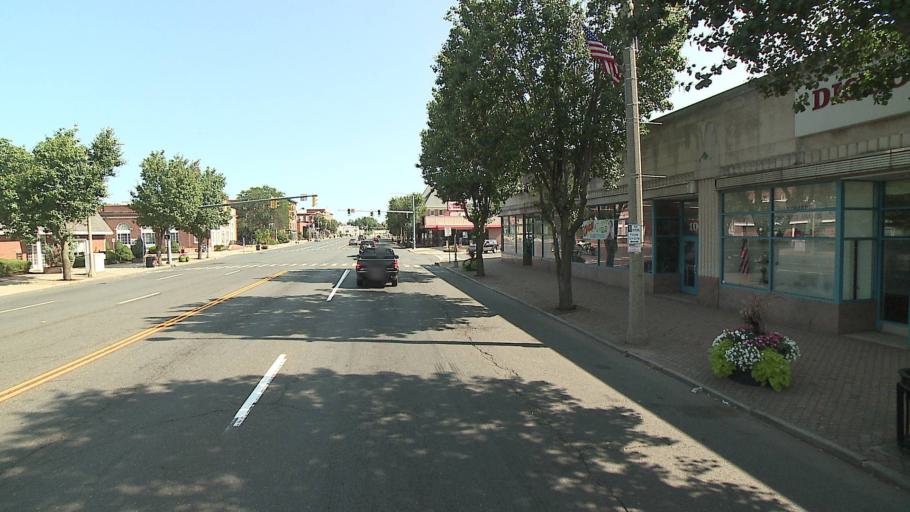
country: US
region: Connecticut
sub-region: Hartford County
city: East Hartford
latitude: 41.7719
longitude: -72.6421
